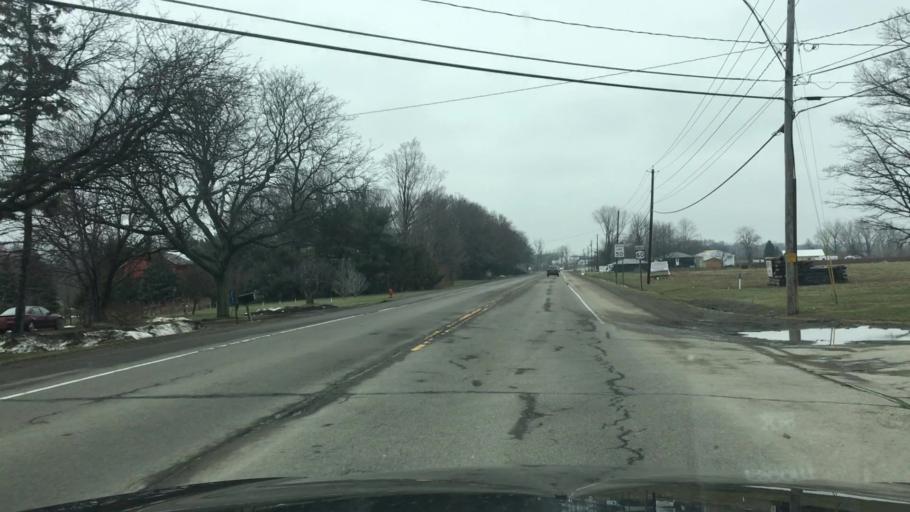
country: US
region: New York
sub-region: Chautauqua County
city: Fredonia
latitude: 42.4258
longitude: -79.3062
